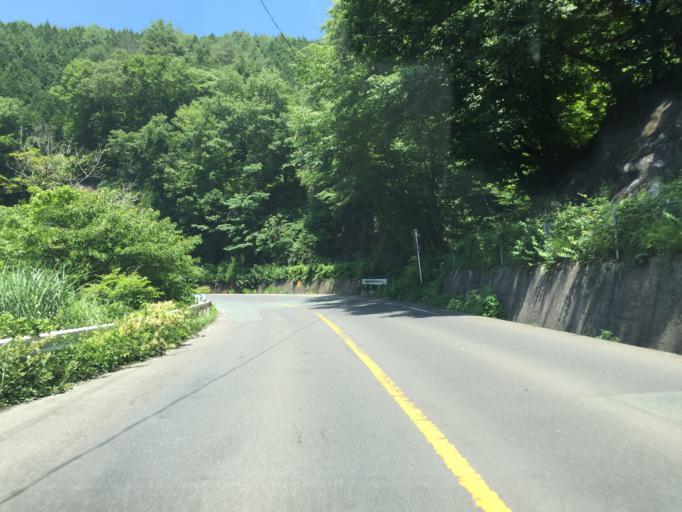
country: JP
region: Miyagi
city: Marumori
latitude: 37.7715
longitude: 140.7788
